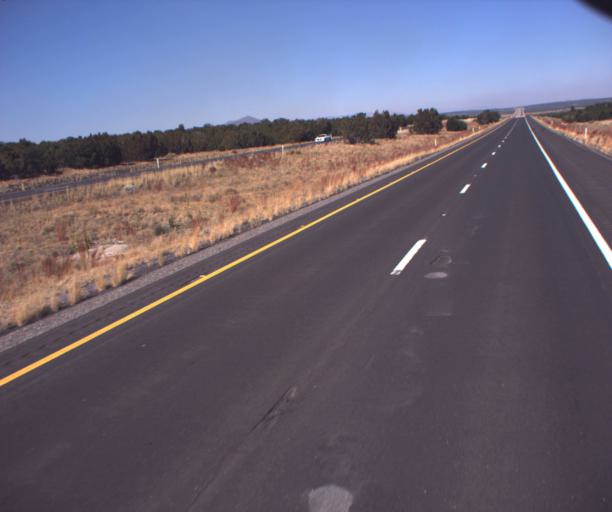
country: US
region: Arizona
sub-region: Coconino County
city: Flagstaff
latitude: 35.4140
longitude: -111.5724
